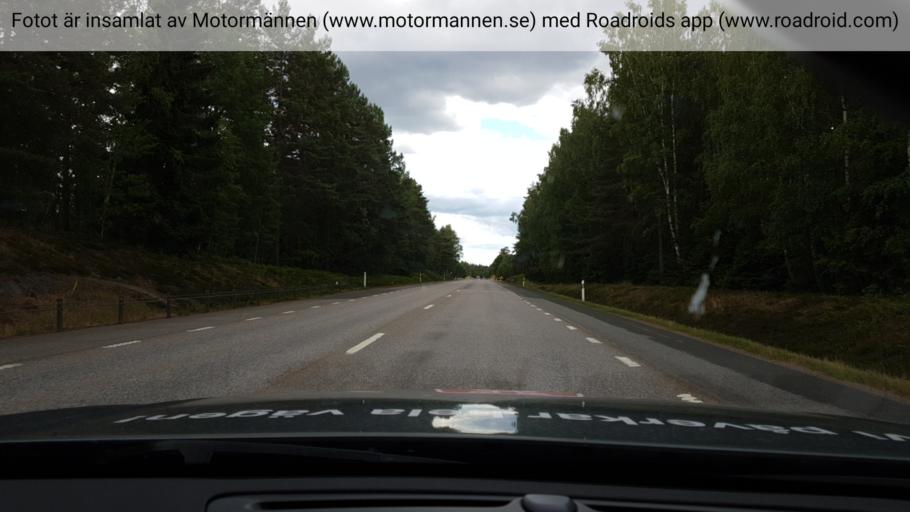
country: SE
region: Kalmar
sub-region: Vasterviks Kommun
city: Ankarsrum
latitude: 57.6888
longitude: 16.4401
